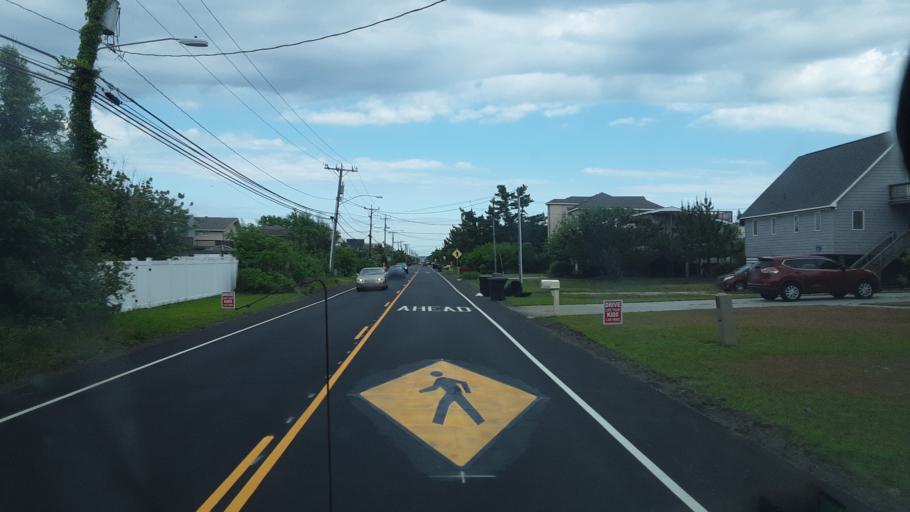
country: US
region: Virginia
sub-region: City of Virginia Beach
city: Virginia Beach
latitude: 36.7238
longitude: -75.9368
